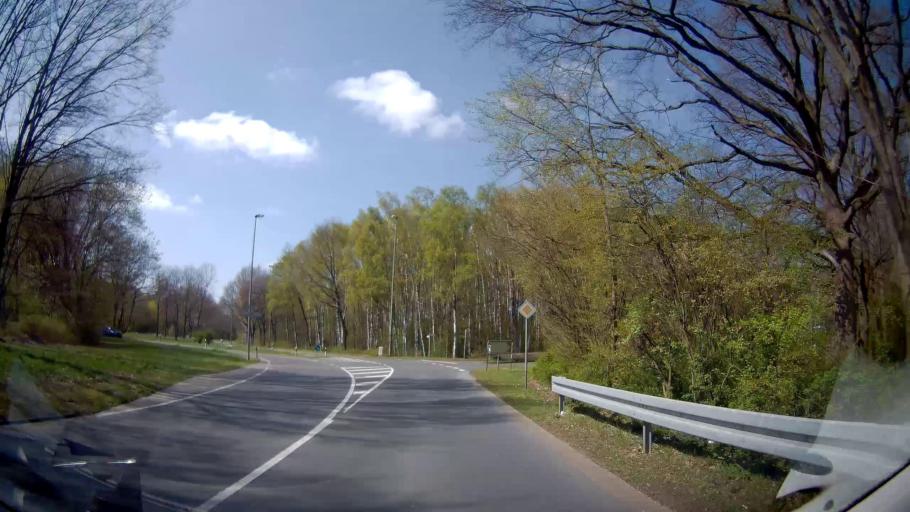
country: DE
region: North Rhine-Westphalia
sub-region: Regierungsbezirk Munster
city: Klein Reken
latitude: 51.7246
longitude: 7.0320
